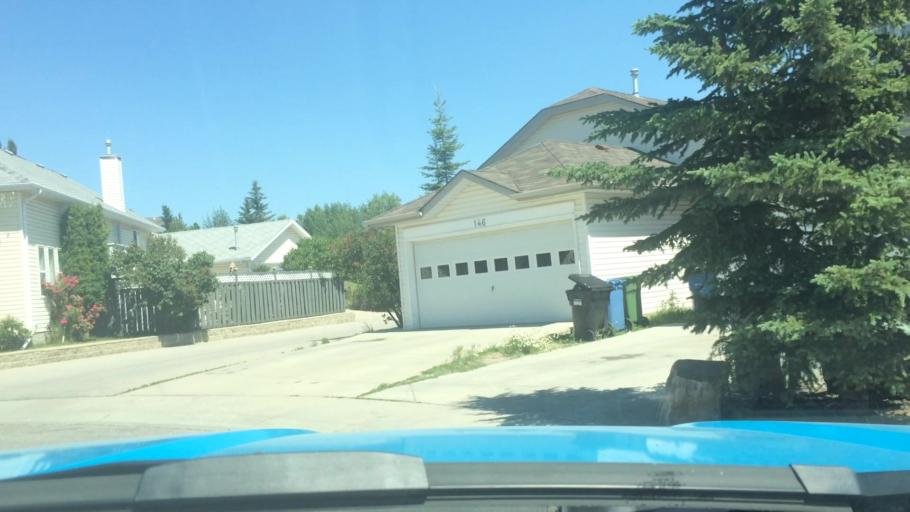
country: CA
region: Alberta
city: Calgary
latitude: 51.1287
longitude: -114.2063
